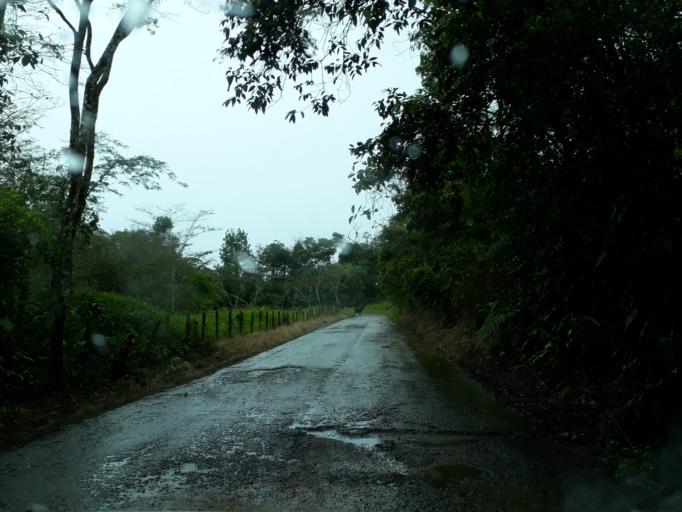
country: CO
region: Cundinamarca
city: Medina
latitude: 4.6539
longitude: -73.3298
